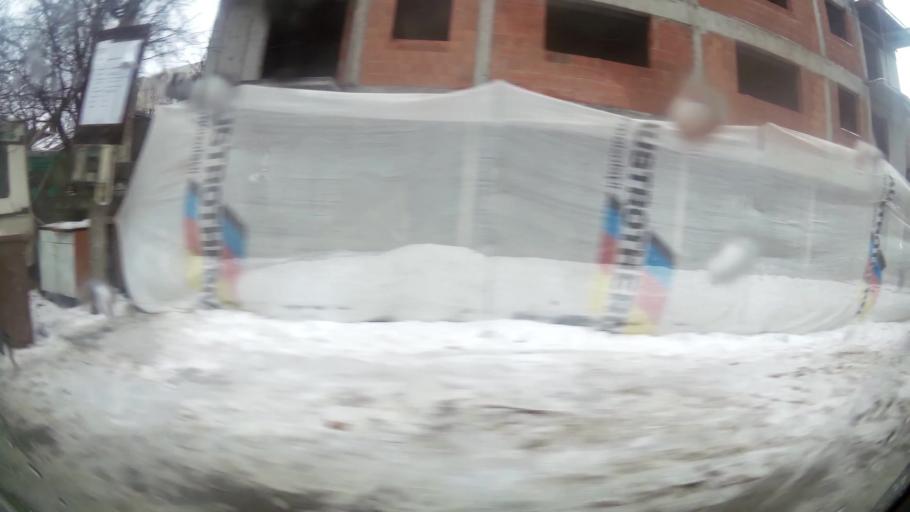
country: RO
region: Ilfov
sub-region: Comuna Chiajna
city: Rosu
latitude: 44.4302
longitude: 26.0109
